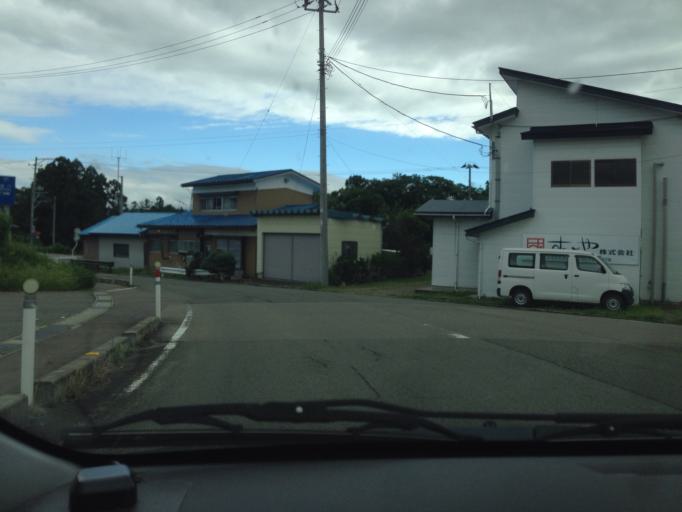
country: JP
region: Fukushima
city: Kitakata
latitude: 37.5777
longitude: 139.9453
